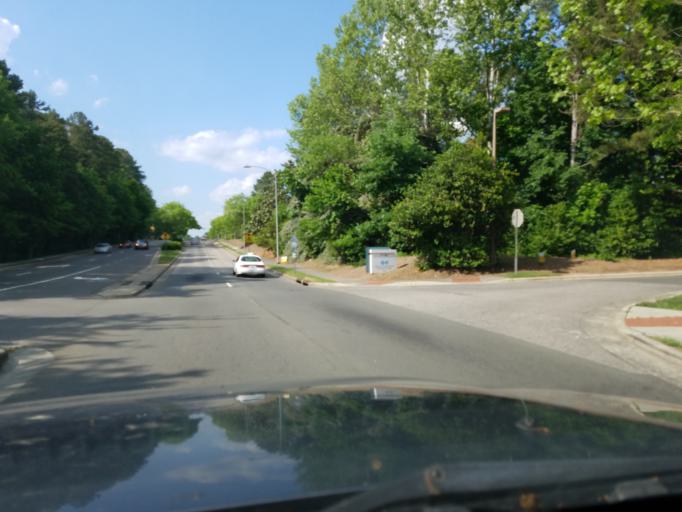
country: US
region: North Carolina
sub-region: Durham County
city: Durham
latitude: 35.9524
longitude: -78.9662
